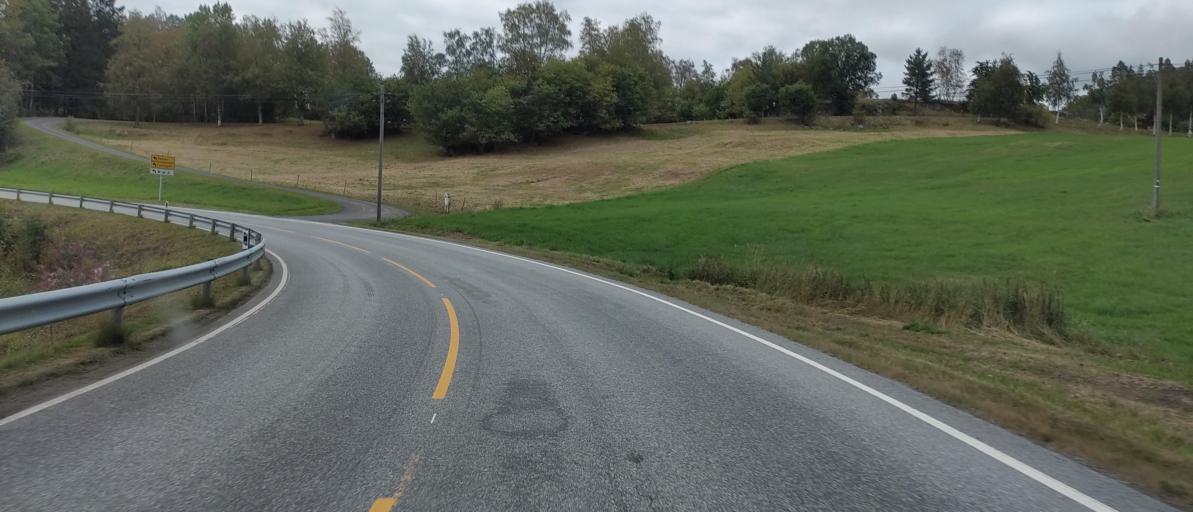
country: NO
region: More og Romsdal
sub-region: Rauma
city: Andalsnes
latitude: 62.5857
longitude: 7.5408
